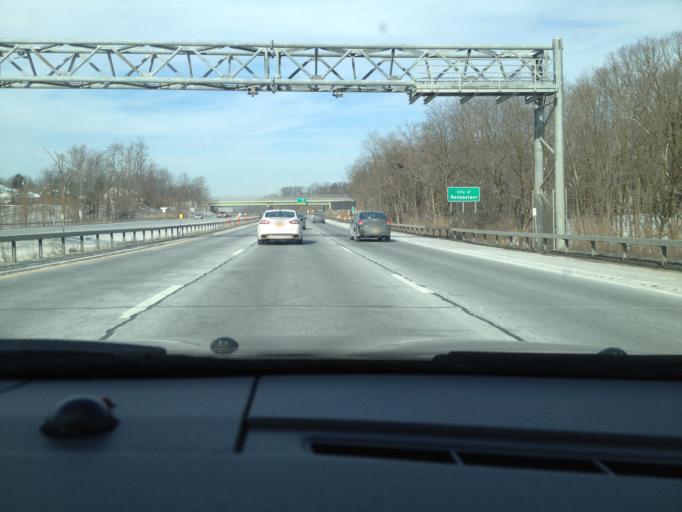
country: US
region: New York
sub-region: Rensselaer County
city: Rensselaer
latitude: 42.6575
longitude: -73.7200
